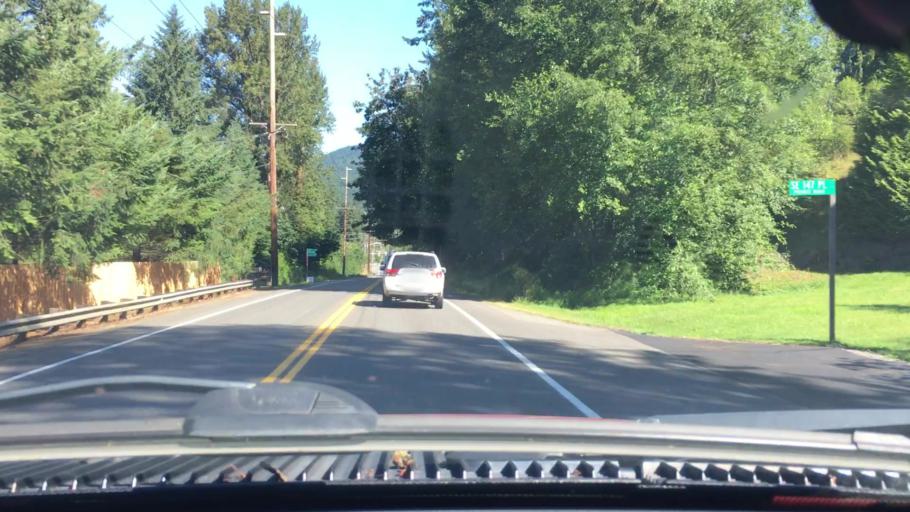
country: US
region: Washington
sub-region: King County
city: Mirrormont
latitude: 47.4696
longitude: -122.0201
